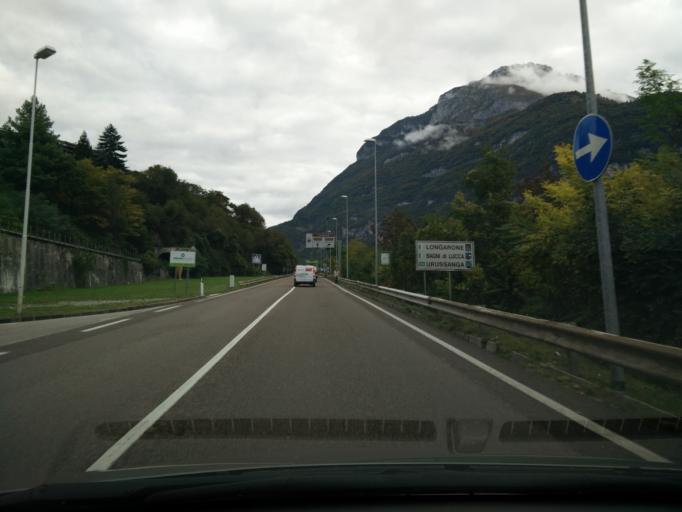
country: IT
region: Veneto
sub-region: Provincia di Belluno
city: Longarone
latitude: 46.2619
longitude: 12.3017
